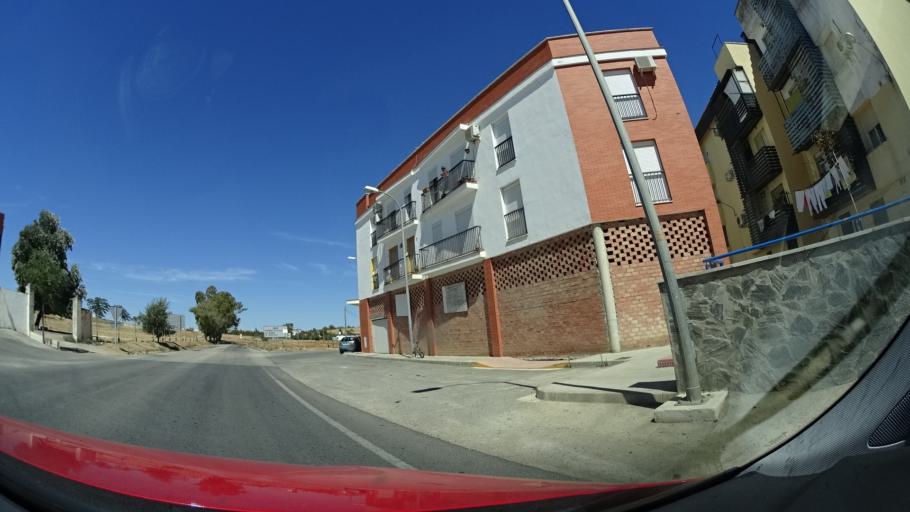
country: ES
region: Andalusia
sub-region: Provincia de Malaga
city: Campillos
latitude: 37.0539
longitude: -4.8639
